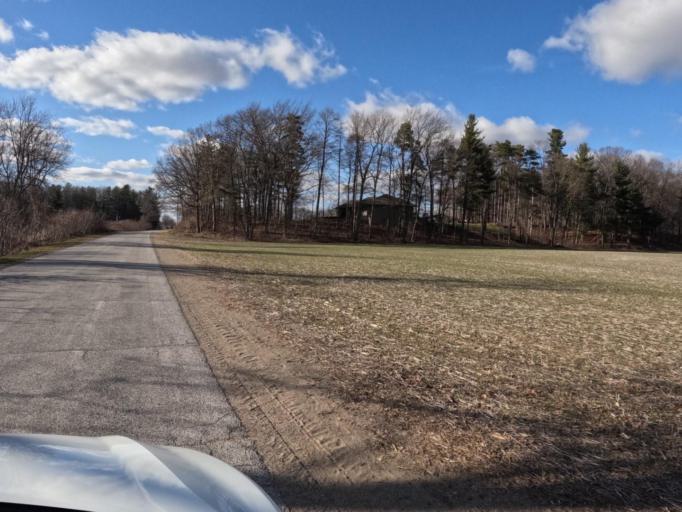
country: CA
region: Ontario
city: Norfolk County
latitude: 42.8079
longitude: -80.5595
